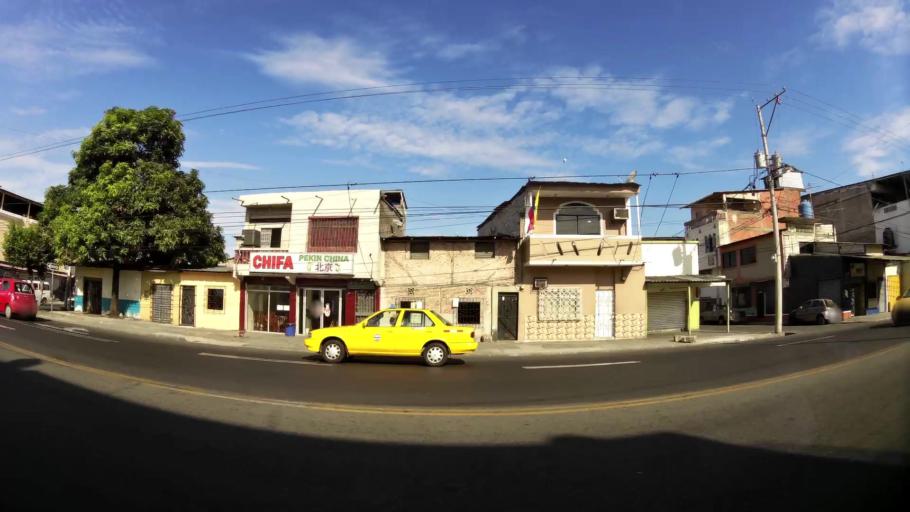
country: EC
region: Guayas
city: Guayaquil
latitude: -2.2034
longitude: -79.9176
